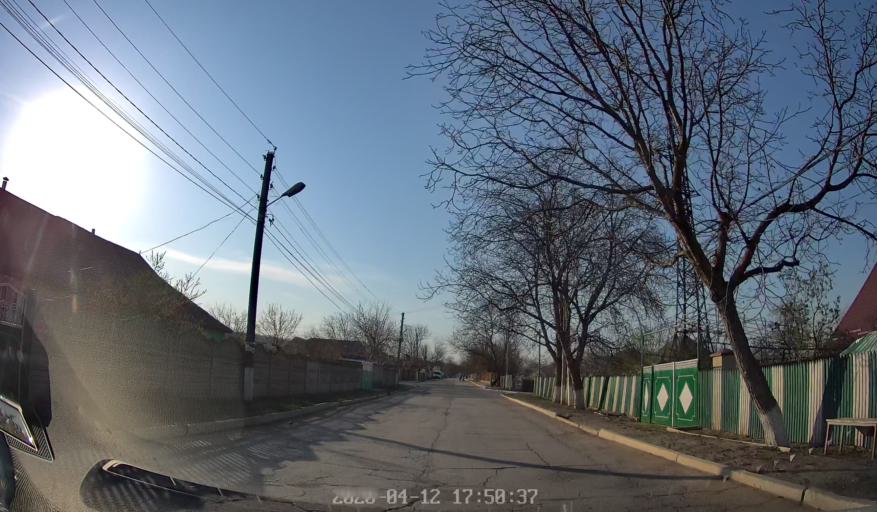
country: MD
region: Telenesti
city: Cocieri
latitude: 47.3769
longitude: 29.1257
